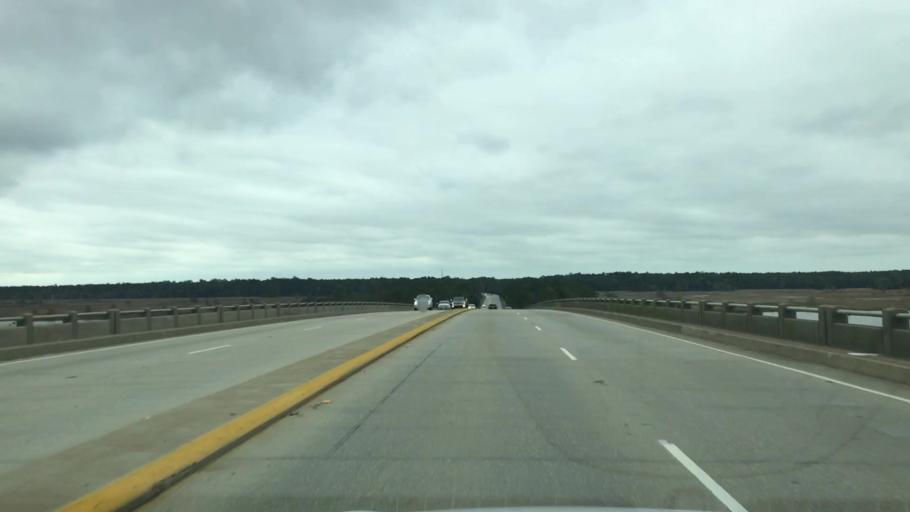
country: US
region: South Carolina
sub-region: Georgetown County
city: Georgetown
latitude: 33.3656
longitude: -79.2529
